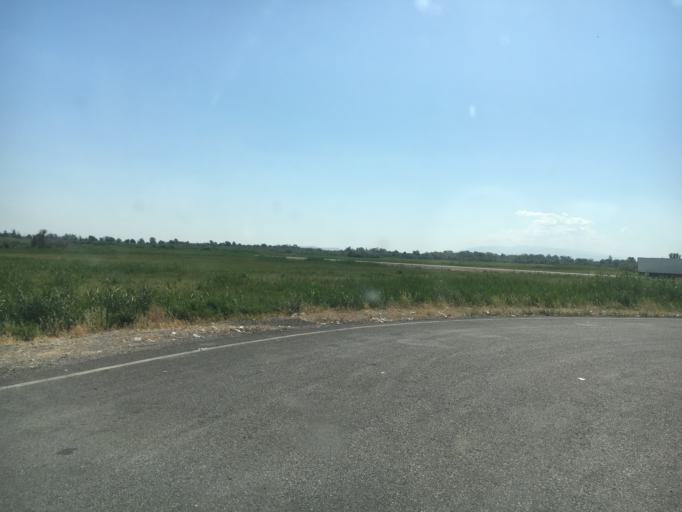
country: KZ
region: Zhambyl
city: Taraz
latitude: 42.9860
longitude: 71.2200
